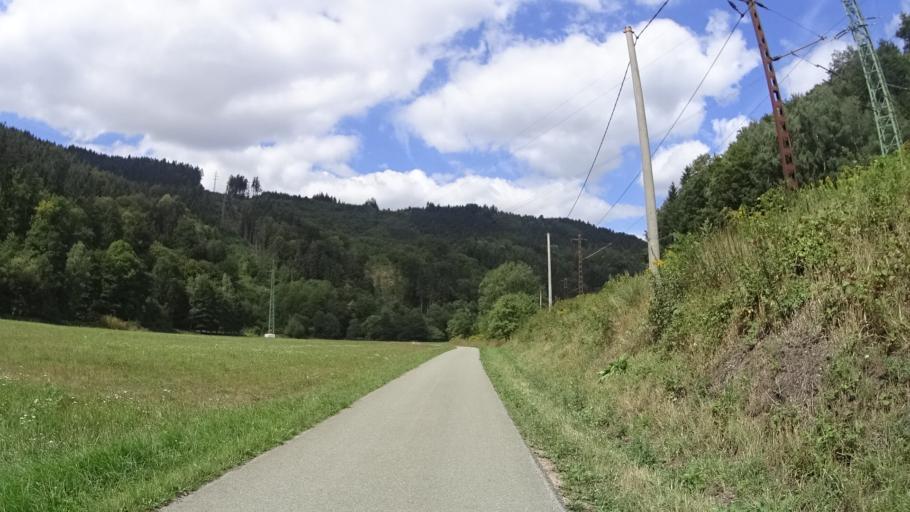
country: CZ
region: Pardubicky
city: Horni Sloupnice
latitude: 49.9747
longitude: 16.3375
